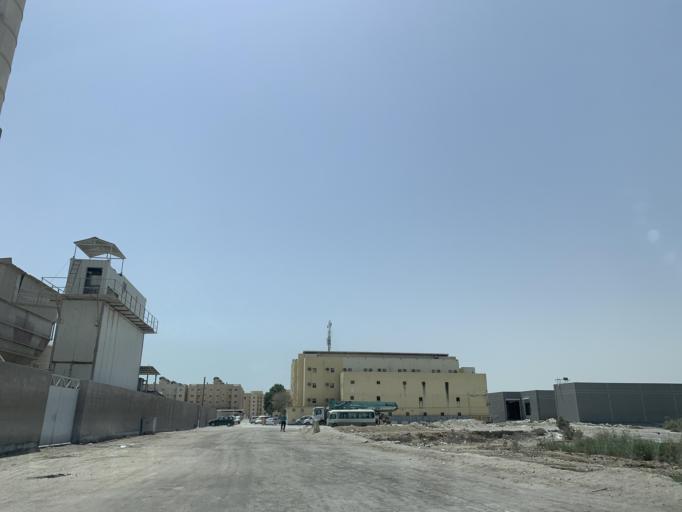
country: BH
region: Northern
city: Sitrah
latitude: 26.1468
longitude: 50.5943
